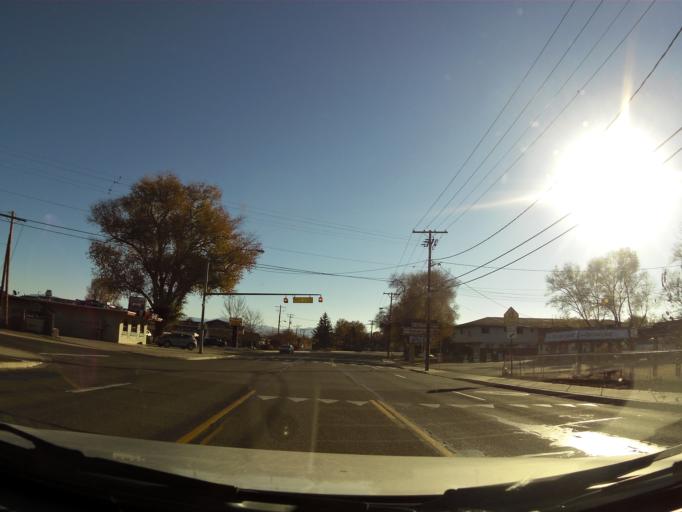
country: US
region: Nevada
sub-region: Douglas County
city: Gardnerville
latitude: 38.9395
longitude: -119.7464
